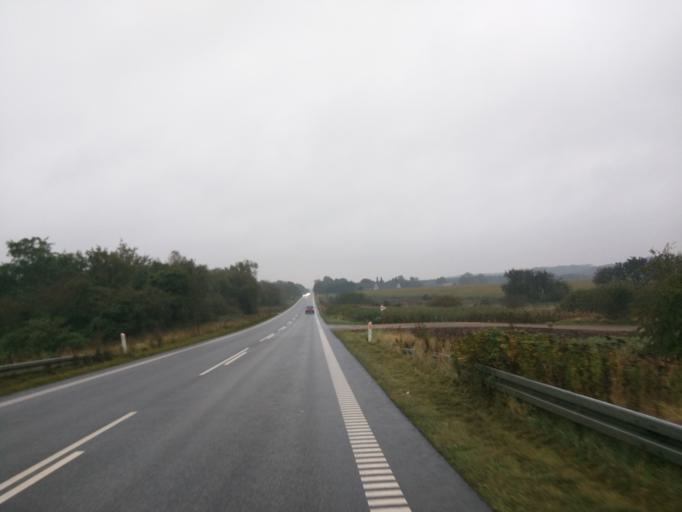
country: DK
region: Central Jutland
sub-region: Viborg Kommune
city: Viborg
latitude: 56.3814
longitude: 9.4429
